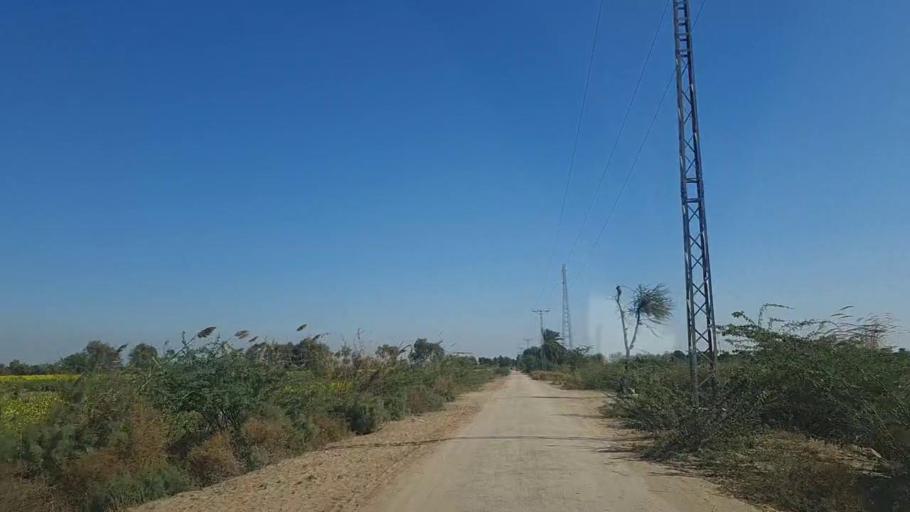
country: PK
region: Sindh
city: Khadro
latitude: 26.1774
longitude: 68.8249
